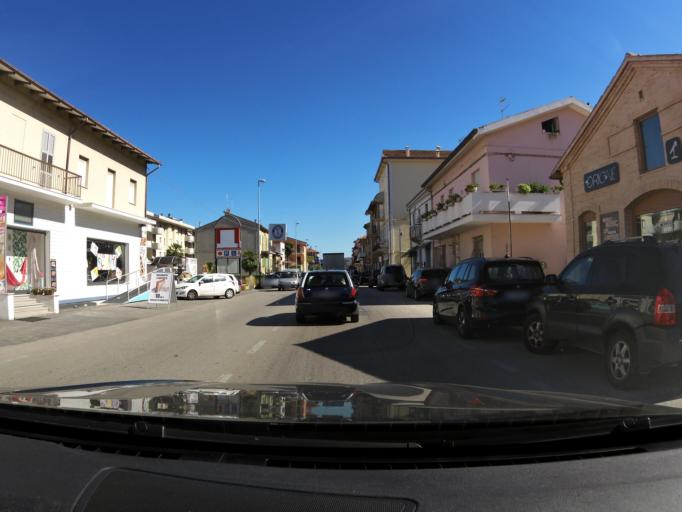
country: IT
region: The Marches
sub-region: Province of Fermo
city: Porto San Giorgio
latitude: 43.1737
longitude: 13.7965
